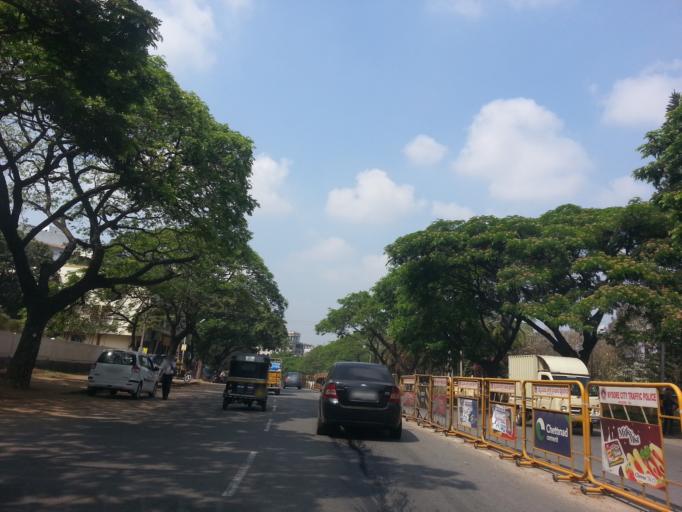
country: IN
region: Karnataka
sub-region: Mysore
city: Mysore
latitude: 12.3319
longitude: 76.6479
